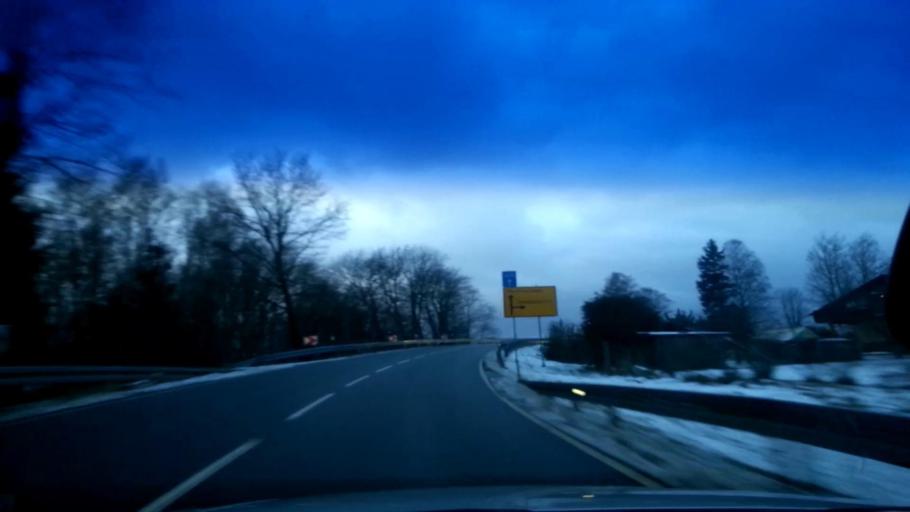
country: DE
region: Bavaria
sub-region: Upper Franconia
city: Marktleuthen
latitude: 50.1422
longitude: 12.0173
